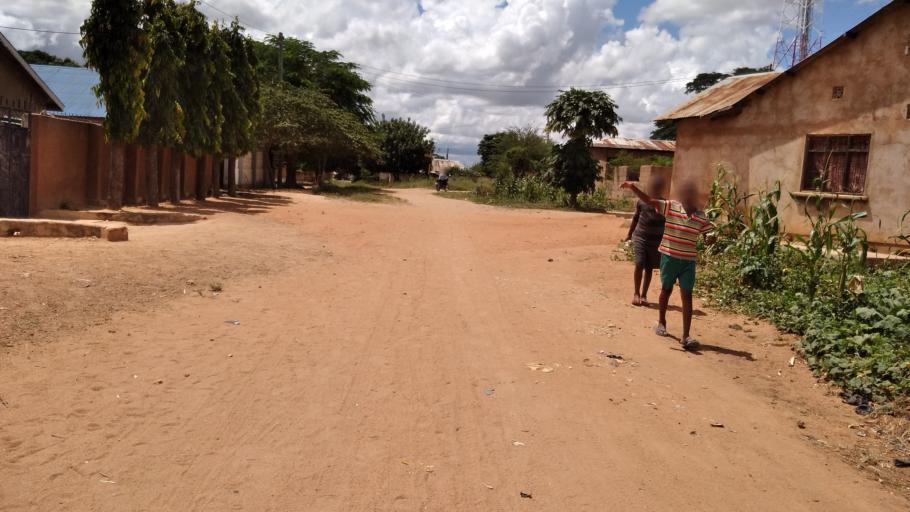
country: TZ
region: Dodoma
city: Dodoma
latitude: -6.1611
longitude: 35.7343
